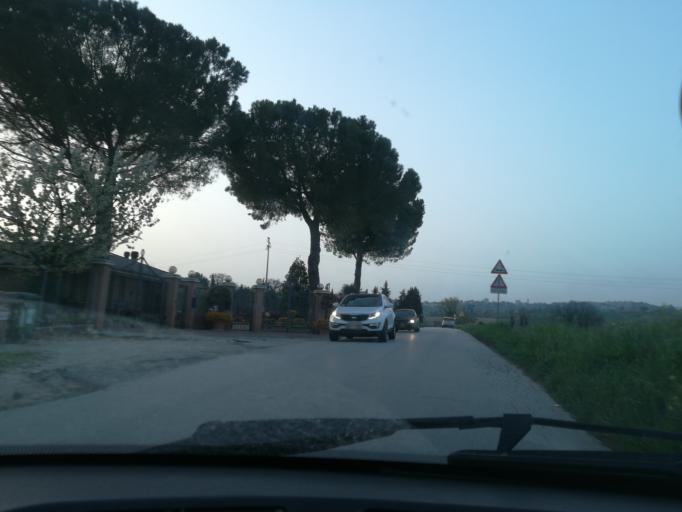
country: IT
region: The Marches
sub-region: Provincia di Macerata
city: Piediripa
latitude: 43.2681
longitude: 13.4627
